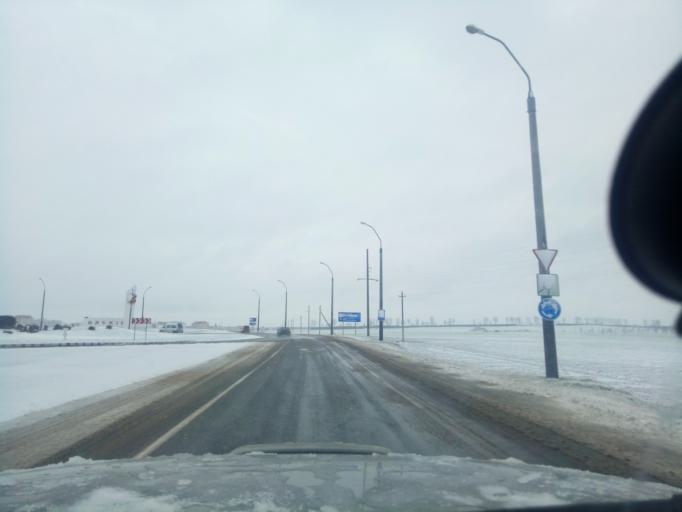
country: BY
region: Minsk
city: Nyasvizh
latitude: 53.2389
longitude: 26.6331
